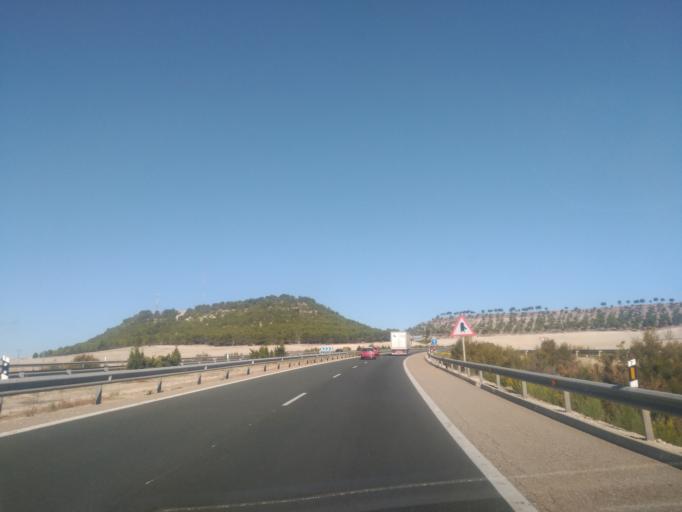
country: ES
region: Castille and Leon
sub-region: Provincia de Valladolid
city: Cisterniga
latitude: 41.6022
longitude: -4.6618
